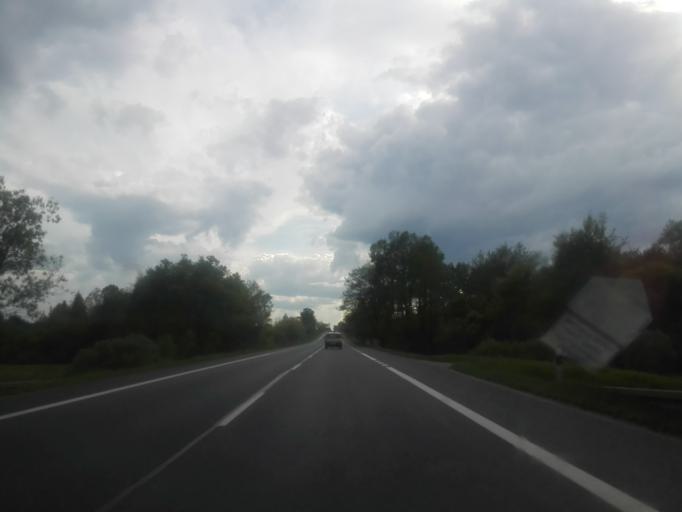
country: PL
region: Podlasie
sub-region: Powiat zambrowski
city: Szumowo
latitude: 52.8761
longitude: 22.0316
